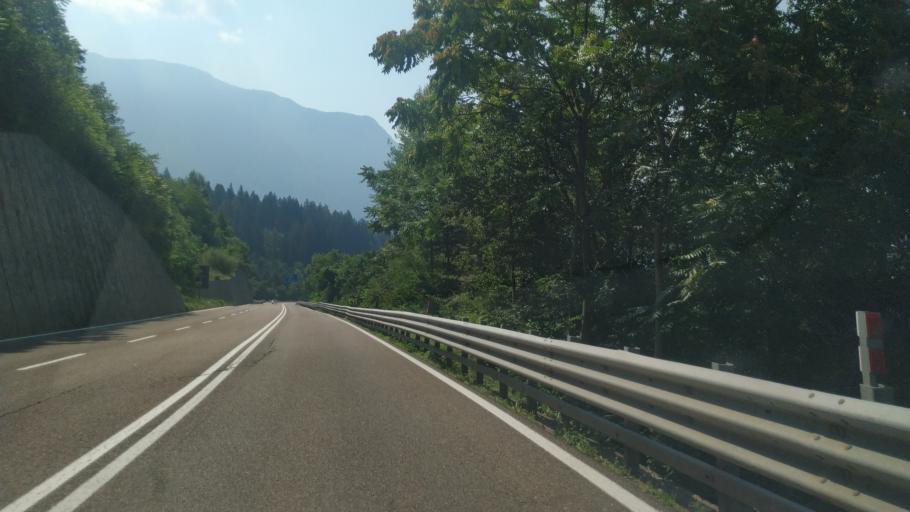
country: IT
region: Trentino-Alto Adige
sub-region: Provincia di Trento
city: Denno
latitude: 46.2808
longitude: 11.0623
